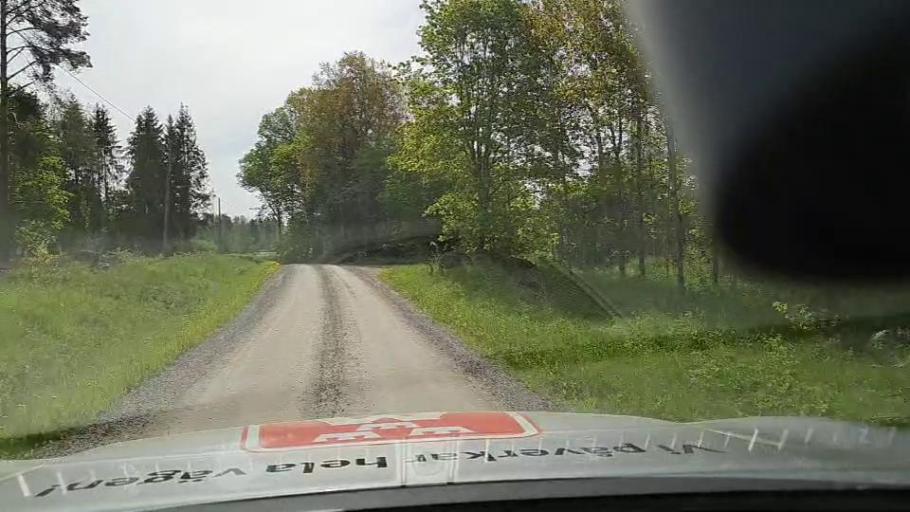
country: SE
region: Soedermanland
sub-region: Flens Kommun
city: Malmkoping
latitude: 59.2614
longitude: 16.8619
